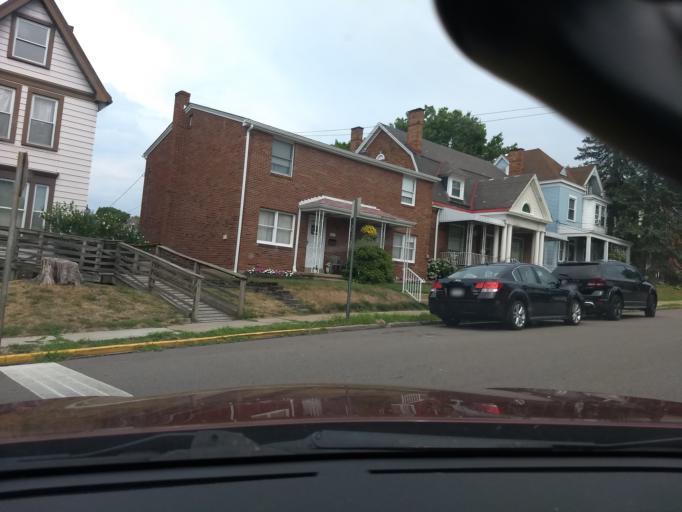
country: US
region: Pennsylvania
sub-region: Allegheny County
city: Bellevue
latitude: 40.4984
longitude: -80.0567
